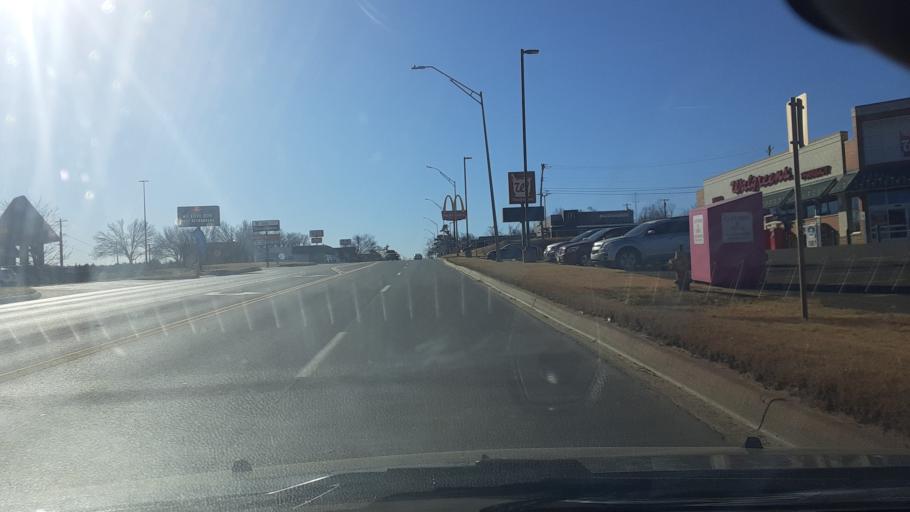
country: US
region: Oklahoma
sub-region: Logan County
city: Guthrie
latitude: 35.8624
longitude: -97.4255
